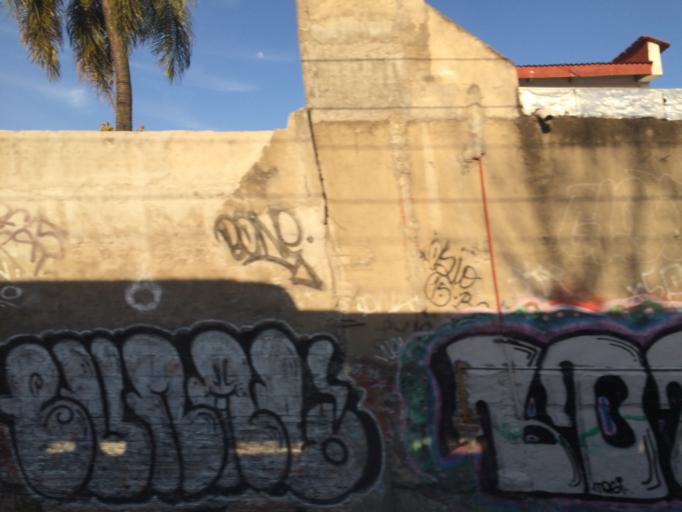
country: AR
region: Buenos Aires
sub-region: Partido de Lomas de Zamora
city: Lomas de Zamora
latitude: -34.7535
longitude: -58.3964
